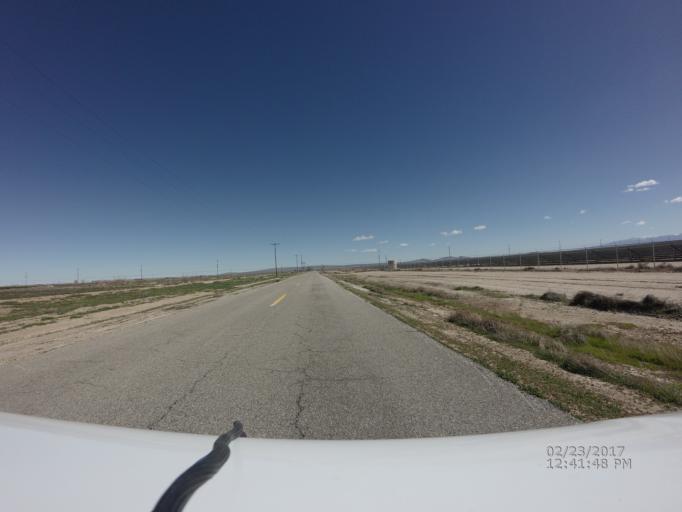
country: US
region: California
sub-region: Los Angeles County
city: Lancaster
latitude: 34.7489
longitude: -117.9732
